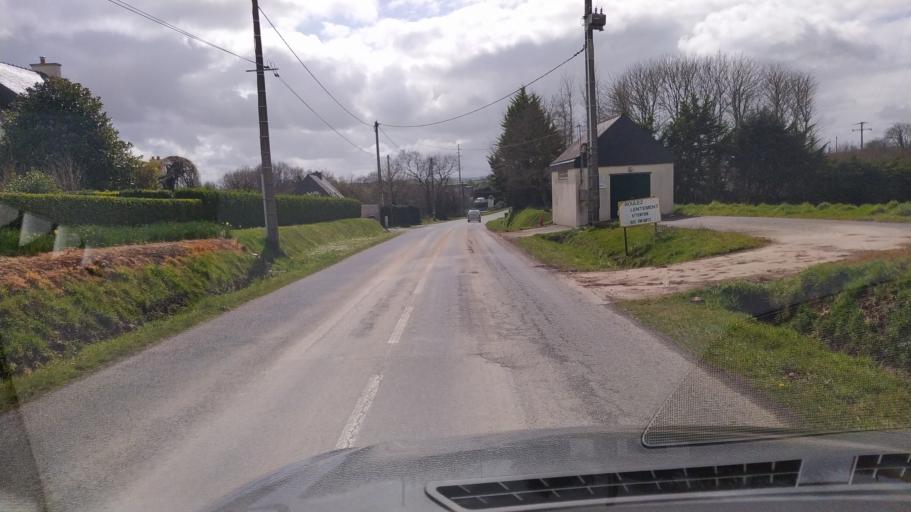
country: FR
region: Brittany
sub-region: Departement du Finistere
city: Bodilis
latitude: 48.5184
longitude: -4.1237
